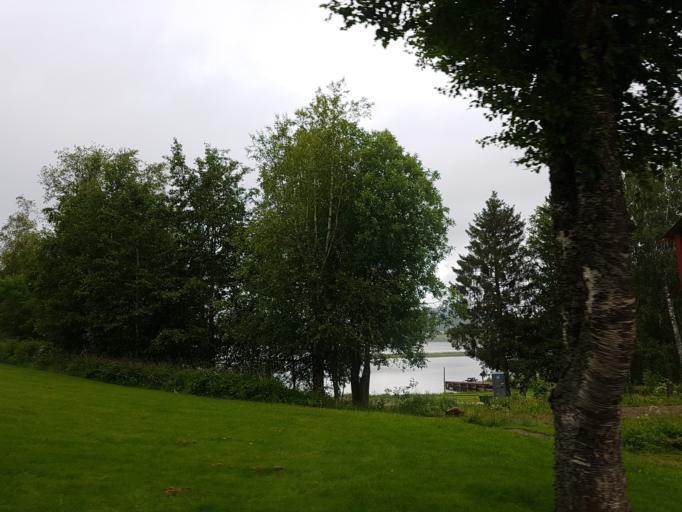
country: NO
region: Sor-Trondelag
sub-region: Selbu
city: Mebonden
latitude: 63.2322
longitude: 11.0308
